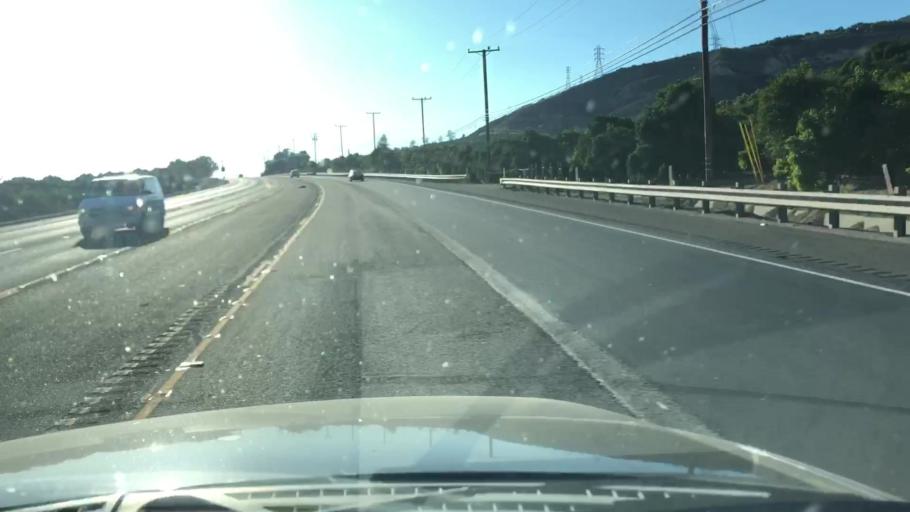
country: US
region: California
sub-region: Ventura County
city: Fillmore
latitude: 34.3971
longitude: -118.8557
